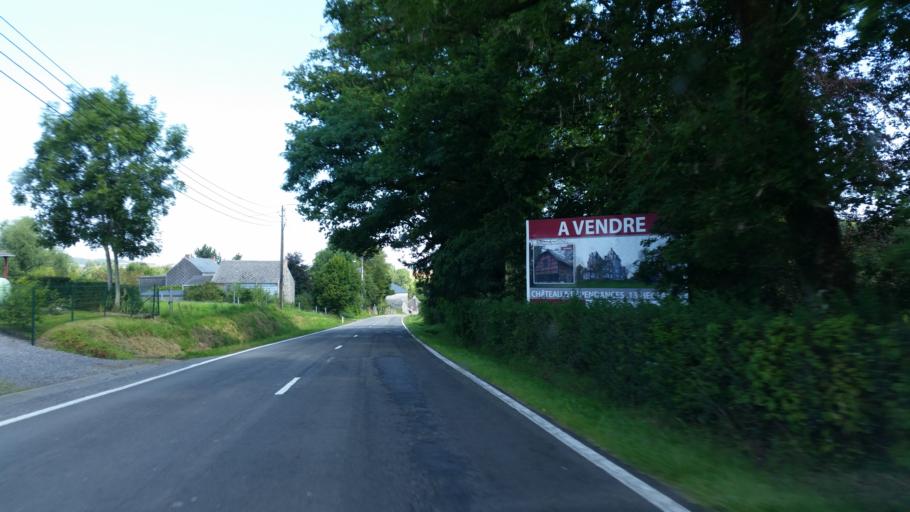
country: BE
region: Wallonia
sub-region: Province de Namur
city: Havelange
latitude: 50.2853
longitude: 5.2553
